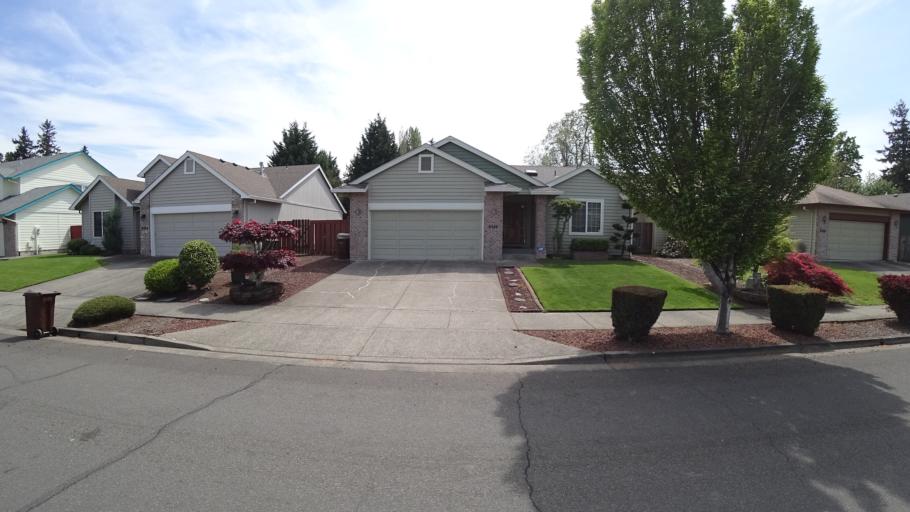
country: US
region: Oregon
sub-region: Washington County
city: Rockcreek
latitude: 45.5146
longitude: -122.9175
